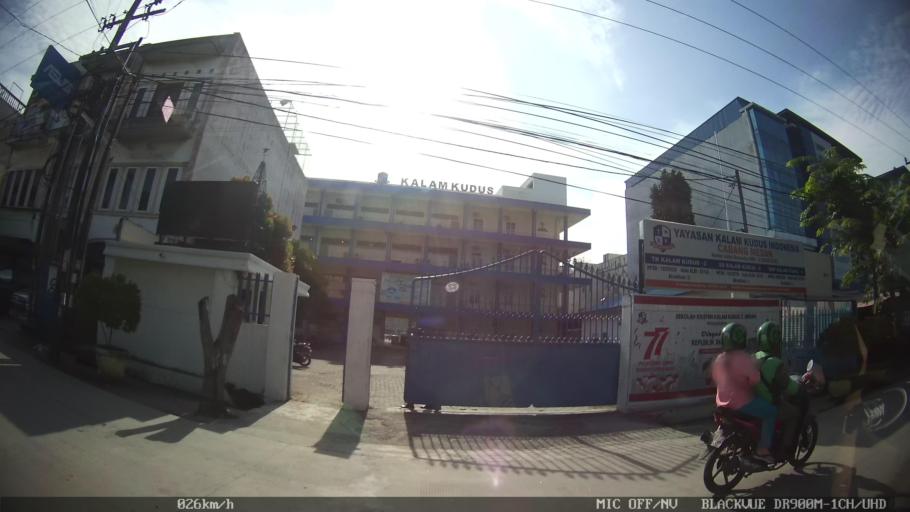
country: ID
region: North Sumatra
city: Medan
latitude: 3.6013
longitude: 98.6452
